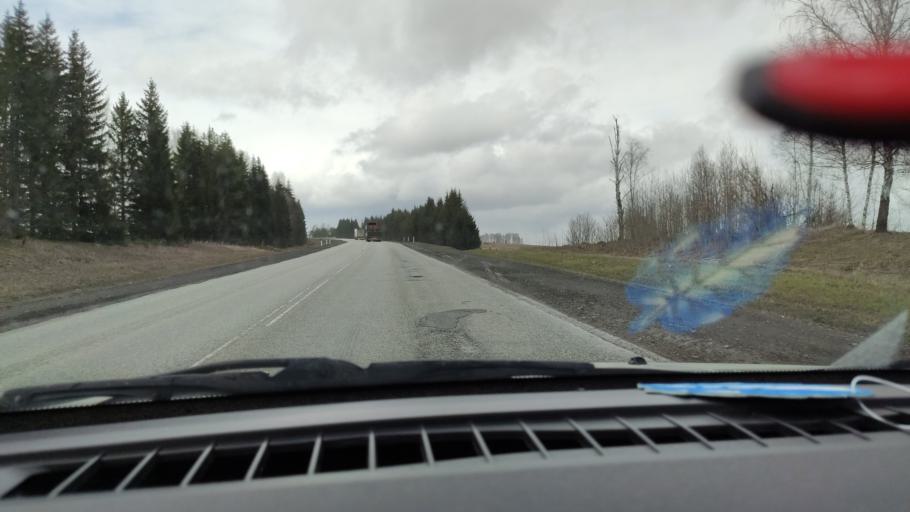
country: RU
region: Perm
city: Kungur
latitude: 57.4713
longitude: 56.7469
